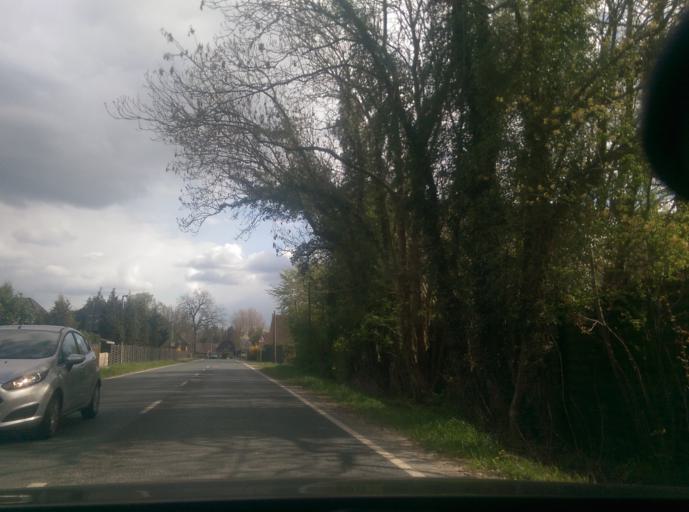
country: DE
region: Lower Saxony
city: Lindwedel
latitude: 52.5565
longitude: 9.6321
